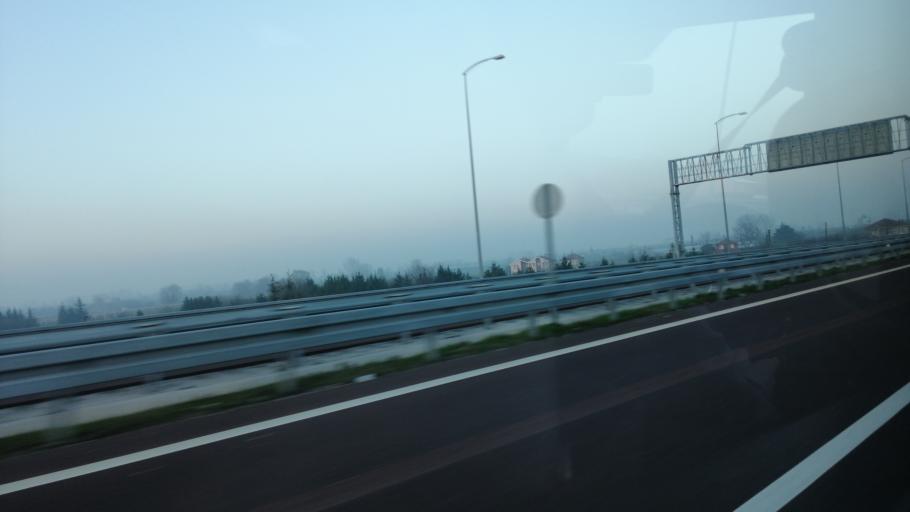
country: TR
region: Yalova
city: Altinova
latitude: 40.6967
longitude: 29.4799
